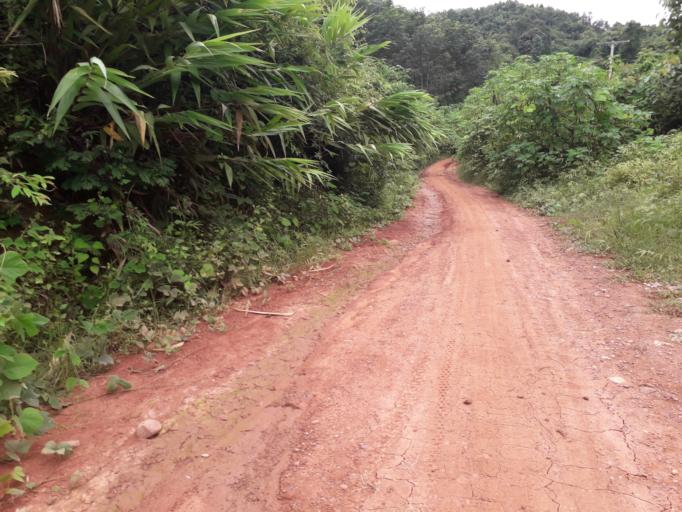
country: CN
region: Yunnan
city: Menglie
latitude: 22.1895
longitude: 101.6980
